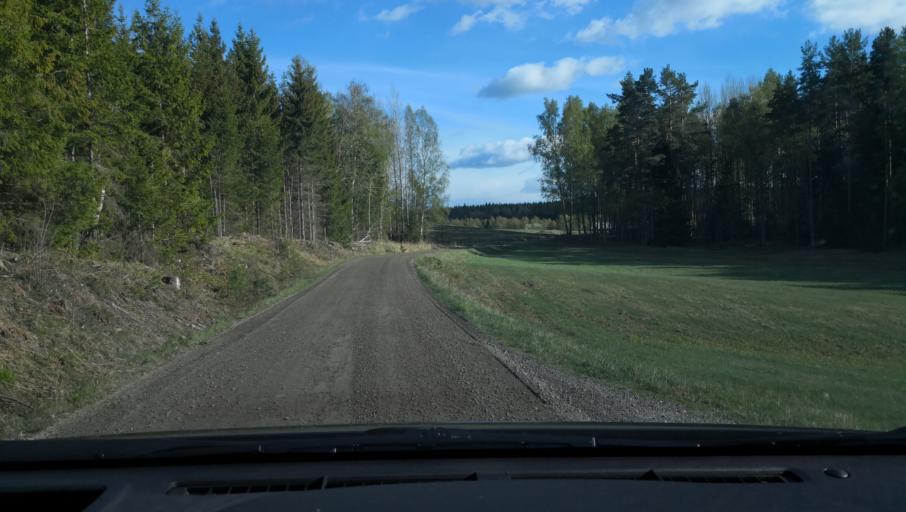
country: SE
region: OErebro
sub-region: Askersunds Kommun
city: Asbro
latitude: 58.8940
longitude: 15.1083
